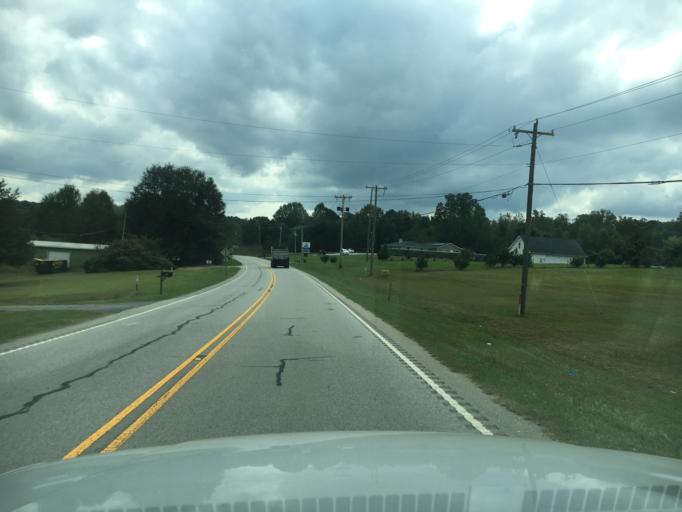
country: US
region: South Carolina
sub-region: Greenville County
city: Greer
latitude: 34.9842
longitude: -82.2459
